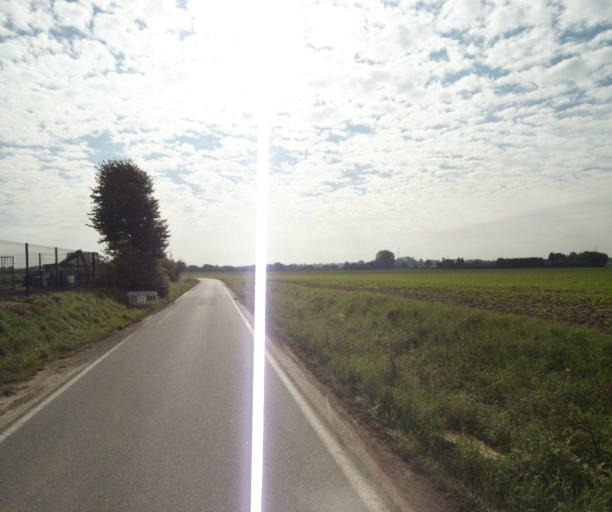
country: FR
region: Nord-Pas-de-Calais
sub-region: Departement du Nord
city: Emmerin
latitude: 50.5871
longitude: 3.0196
